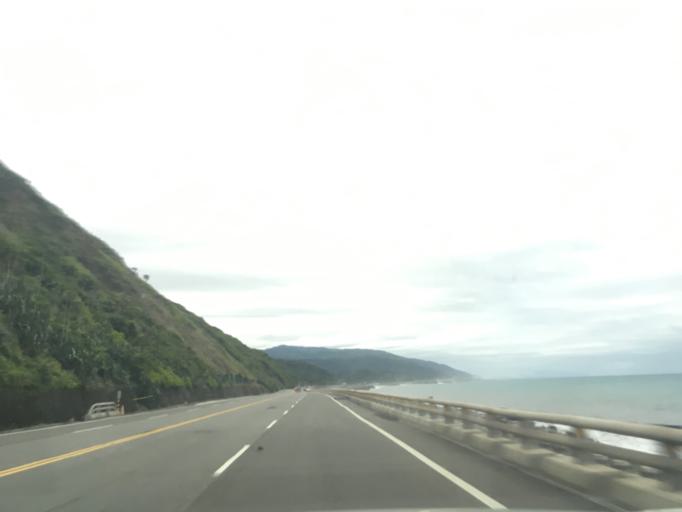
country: TW
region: Taiwan
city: Hengchun
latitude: 22.3146
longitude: 120.8914
